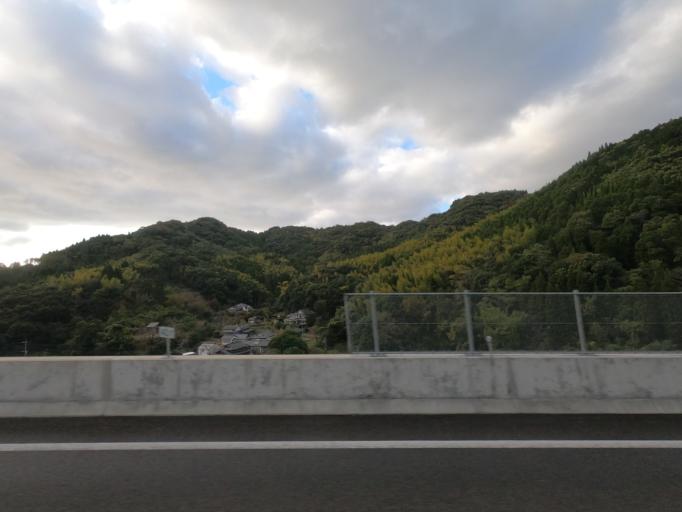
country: JP
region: Kumamoto
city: Minamata
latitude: 32.2223
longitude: 130.4307
